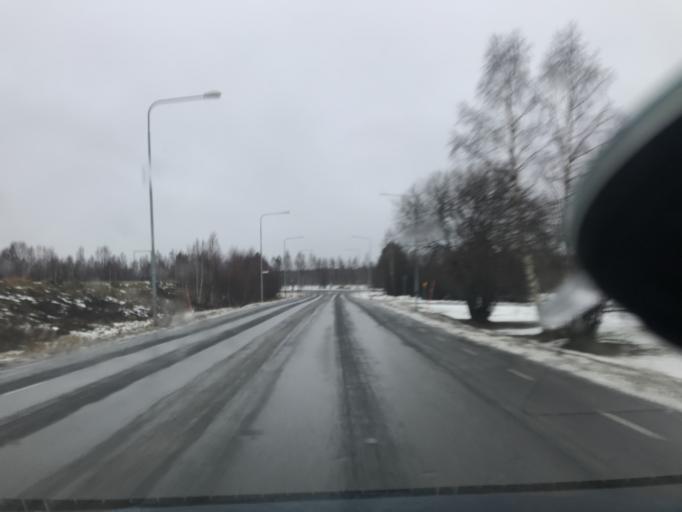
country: SE
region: Norrbotten
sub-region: Lulea Kommun
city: Sodra Sunderbyn
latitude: 65.6587
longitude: 21.9519
